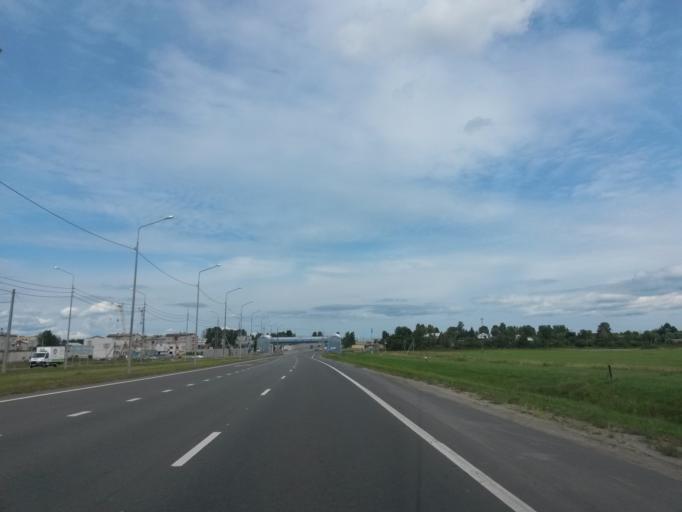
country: RU
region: Jaroslavl
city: Yaroslavl
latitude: 57.6991
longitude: 39.8997
